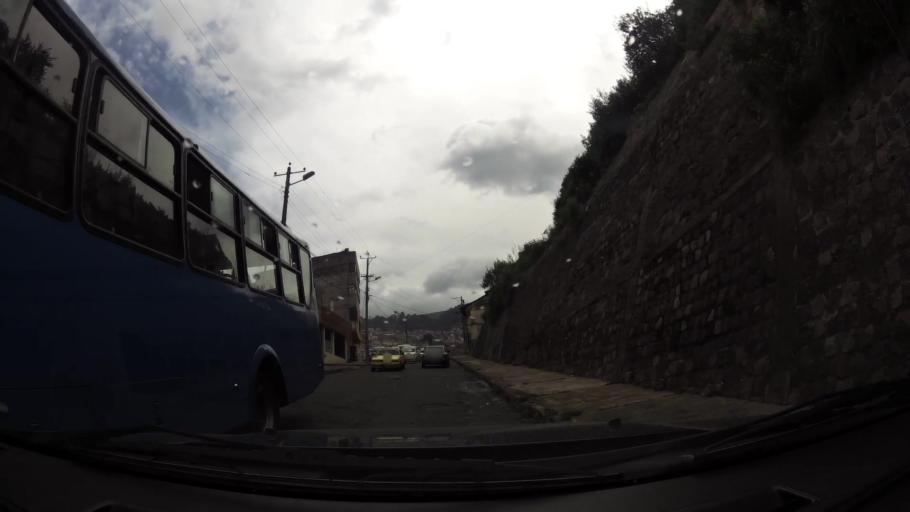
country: EC
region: Pichincha
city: Quito
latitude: -0.2144
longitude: -78.5145
